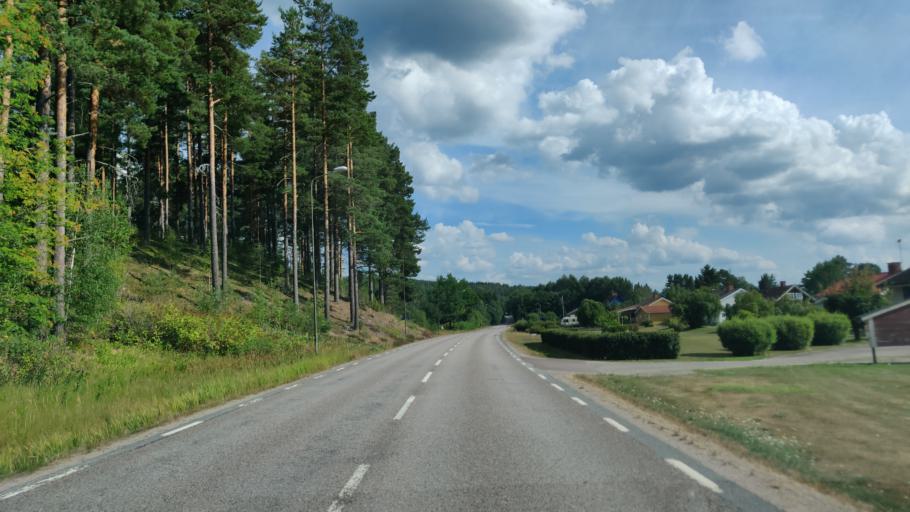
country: SE
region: Vaermland
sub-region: Hagfors Kommun
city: Ekshaerad
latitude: 60.1134
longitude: 13.5649
